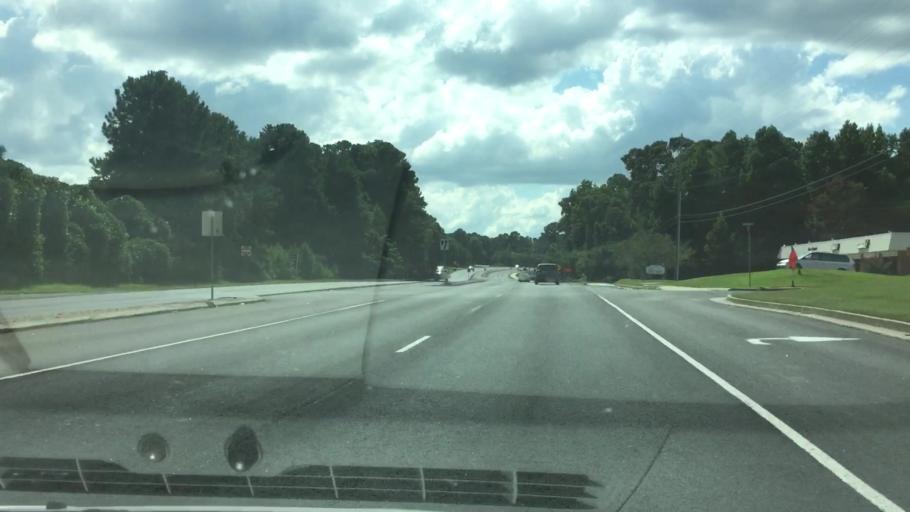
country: US
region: Georgia
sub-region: Fayette County
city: Fayetteville
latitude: 33.4530
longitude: -84.4293
